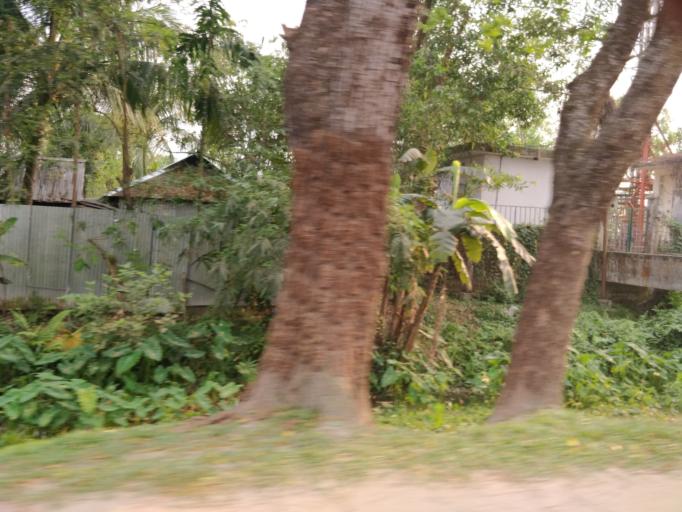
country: IN
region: Tripura
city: Khowai
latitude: 24.1311
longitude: 91.3550
